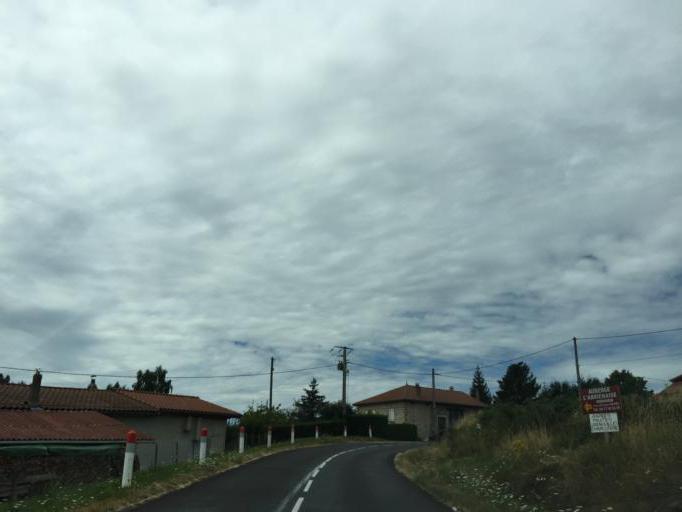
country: FR
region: Rhone-Alpes
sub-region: Departement de la Loire
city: Perigneux
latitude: 45.4060
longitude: 4.1378
